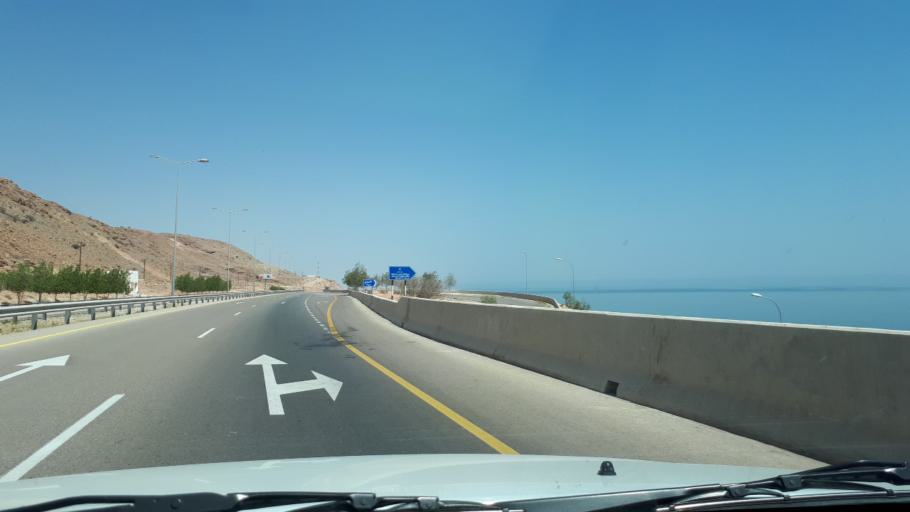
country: OM
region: Ash Sharqiyah
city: Sur
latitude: 22.8272
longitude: 59.2529
